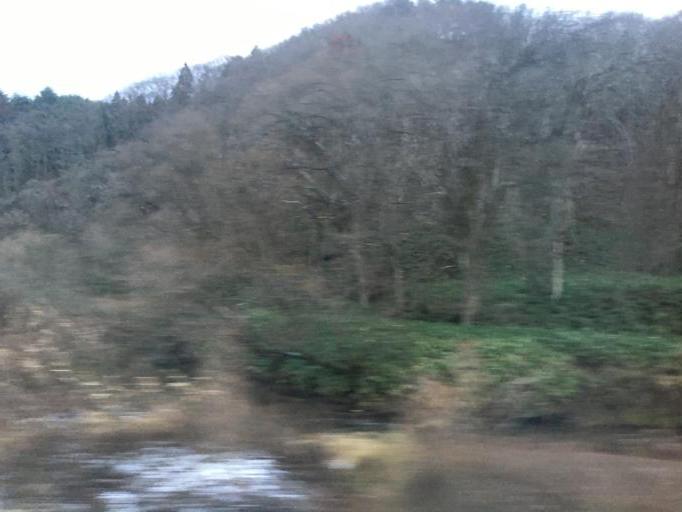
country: JP
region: Aomori
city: Aomori Shi
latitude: 40.8153
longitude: 140.6482
